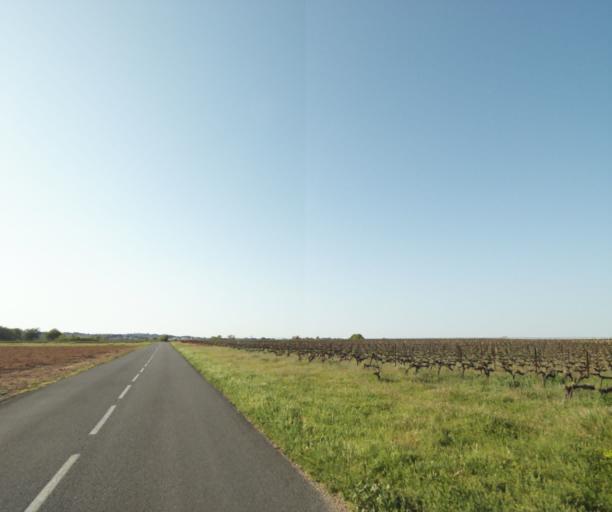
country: FR
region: Languedoc-Roussillon
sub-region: Departement de l'Herault
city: Laverune
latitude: 43.5965
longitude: 3.7940
